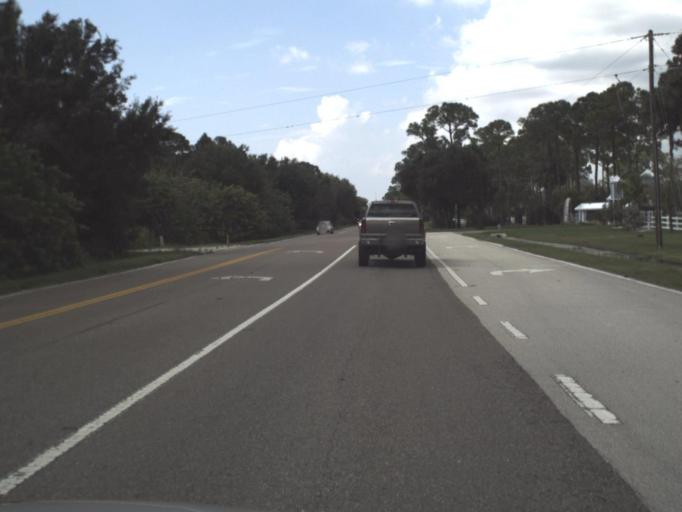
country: US
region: Florida
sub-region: Sarasota County
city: Plantation
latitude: 27.0674
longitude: -82.3213
